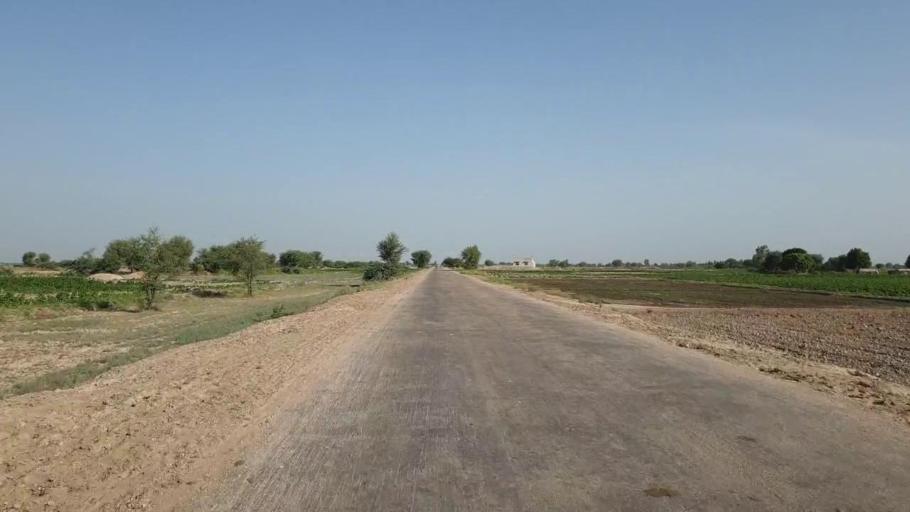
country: PK
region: Sindh
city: Nawabshah
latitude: 26.1442
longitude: 68.4506
